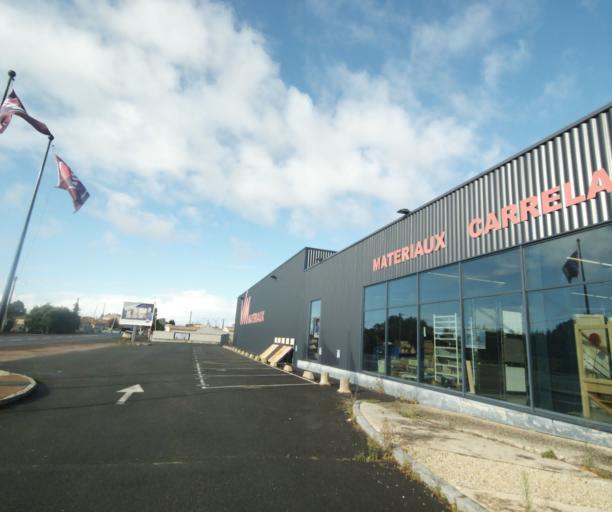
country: FR
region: Poitou-Charentes
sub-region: Departement de la Charente-Maritime
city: Breuil-Magne
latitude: 45.9529
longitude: -0.9387
